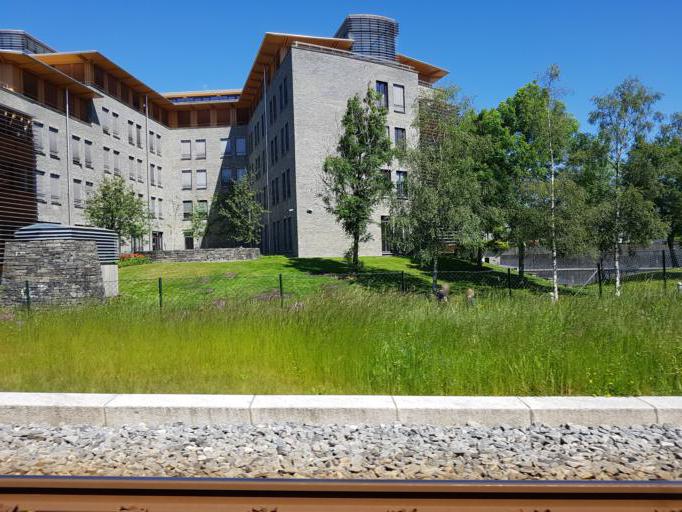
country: NO
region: Hordaland
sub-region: Bergen
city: Ytrebygda
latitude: 60.2878
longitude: 5.2591
